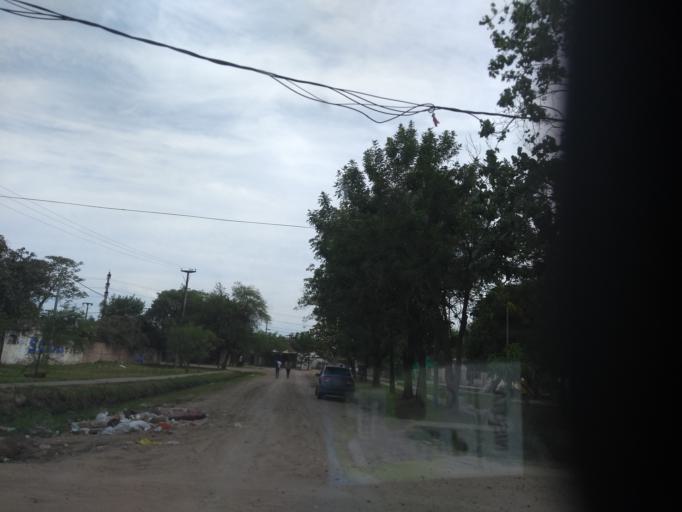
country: AR
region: Chaco
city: Resistencia
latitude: -27.4752
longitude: -58.9720
